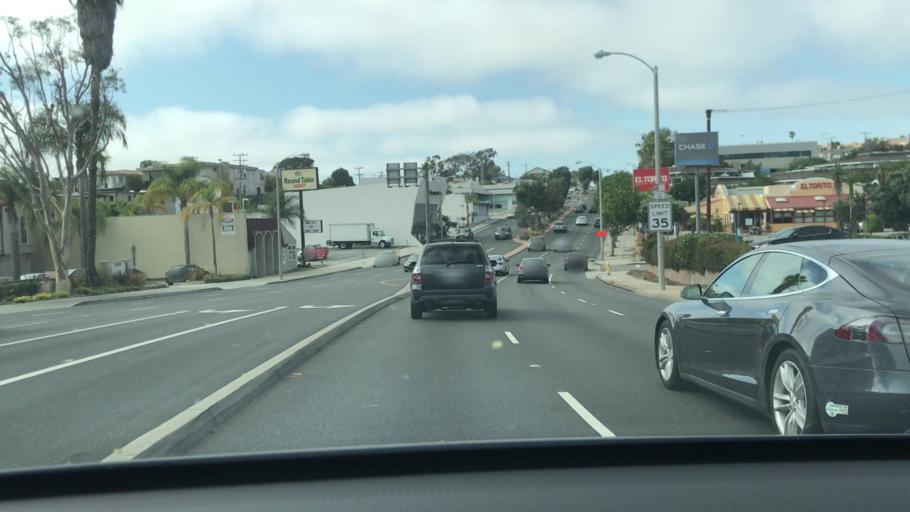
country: US
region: California
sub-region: Los Angeles County
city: Hermosa Beach
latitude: 33.8735
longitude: -118.3959
